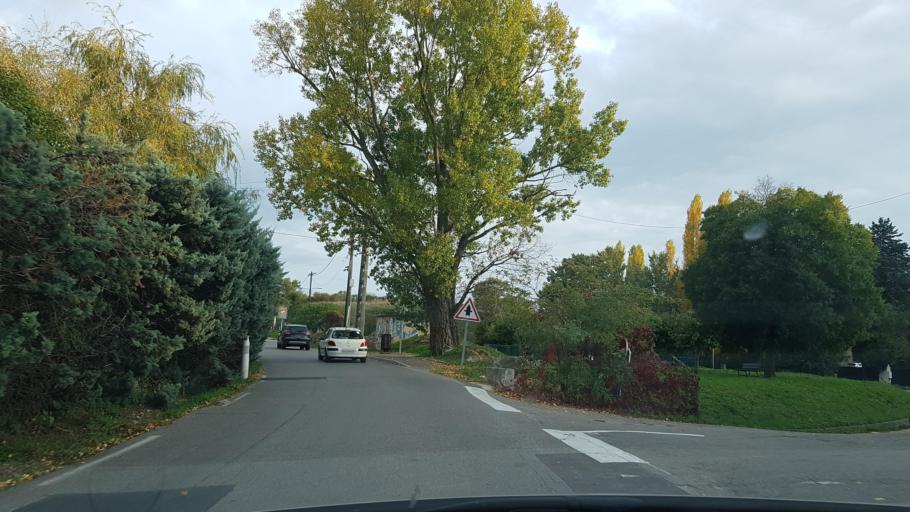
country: FR
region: Provence-Alpes-Cote d'Azur
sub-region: Departement des Bouches-du-Rhone
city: Cabries
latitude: 43.4289
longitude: 5.3833
